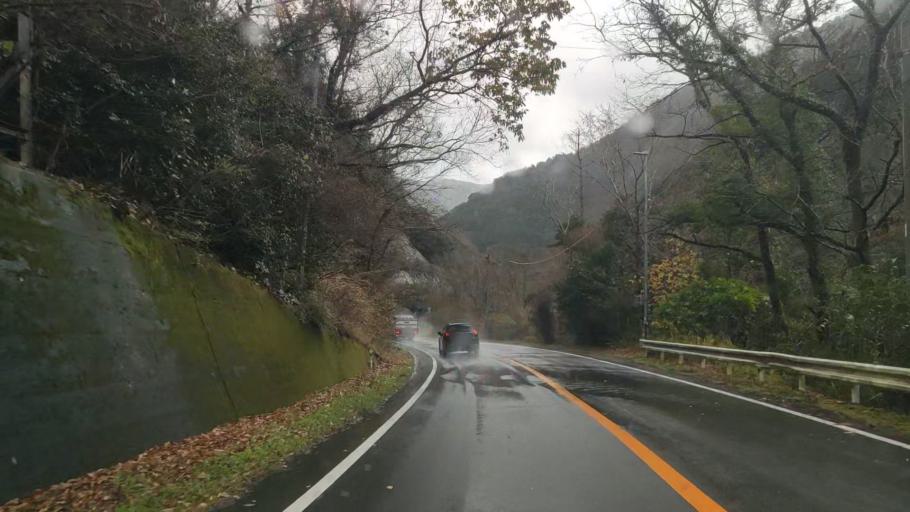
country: JP
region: Tokushima
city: Kamojimacho-jogejima
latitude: 34.1650
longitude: 134.3464
